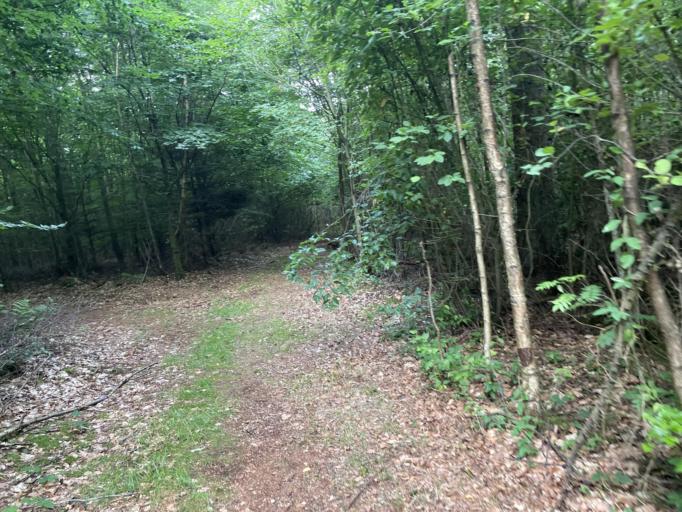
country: DE
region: Schleswig-Holstein
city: Mildstedt
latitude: 54.4724
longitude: 9.1003
